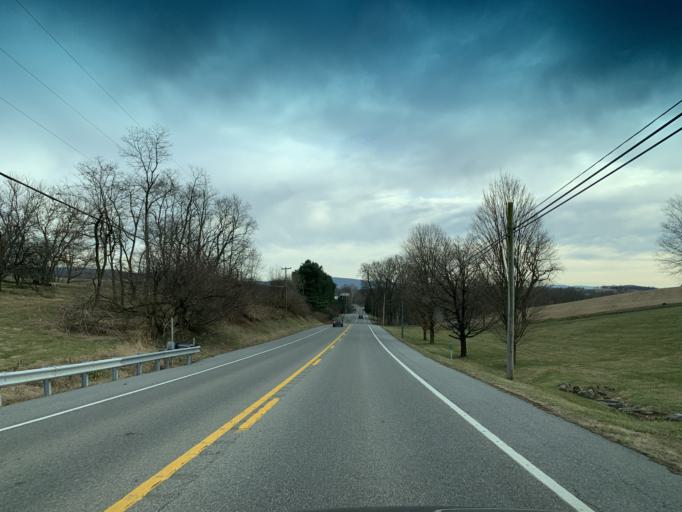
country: US
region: Maryland
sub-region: Washington County
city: Boonsboro
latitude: 39.5562
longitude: -77.6820
